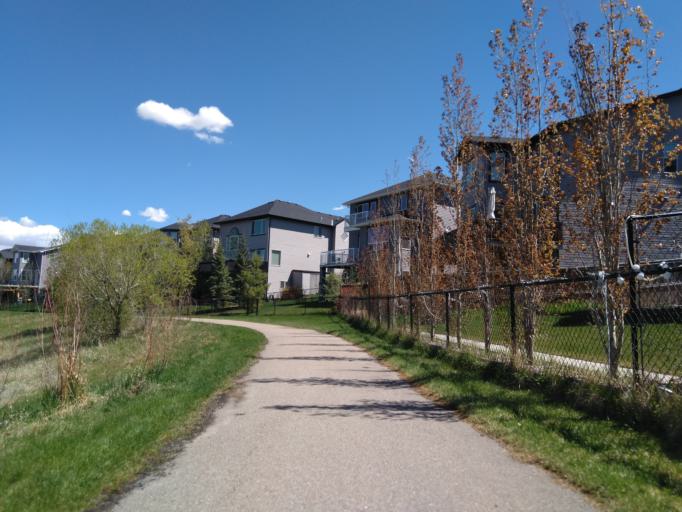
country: CA
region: Alberta
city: Chestermere
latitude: 51.0243
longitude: -113.8341
